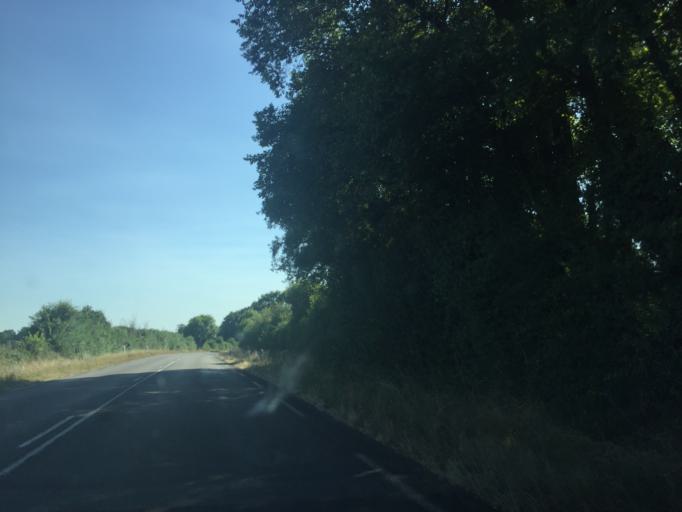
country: FR
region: Poitou-Charentes
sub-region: Departement des Deux-Sevres
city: Melle
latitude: 46.2421
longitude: -0.1040
